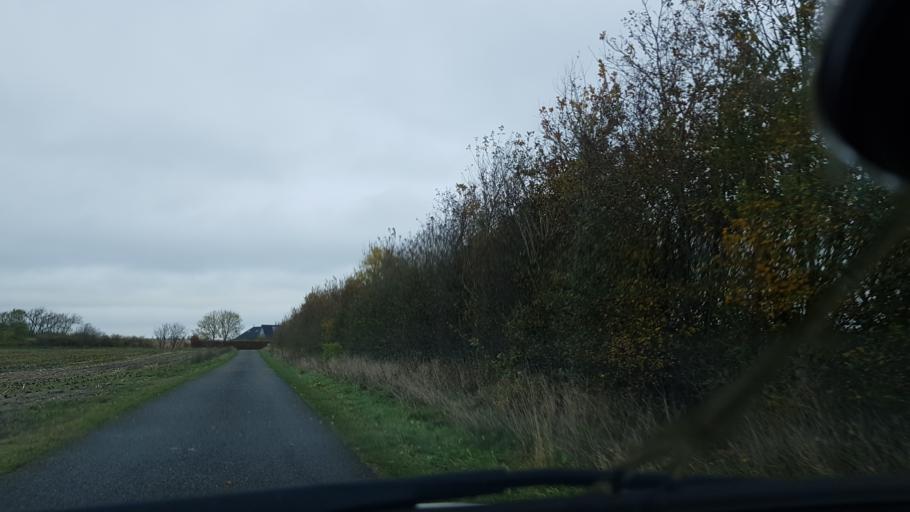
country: DK
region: South Denmark
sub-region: Esbjerg Kommune
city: Ribe
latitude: 55.2591
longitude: 8.8375
